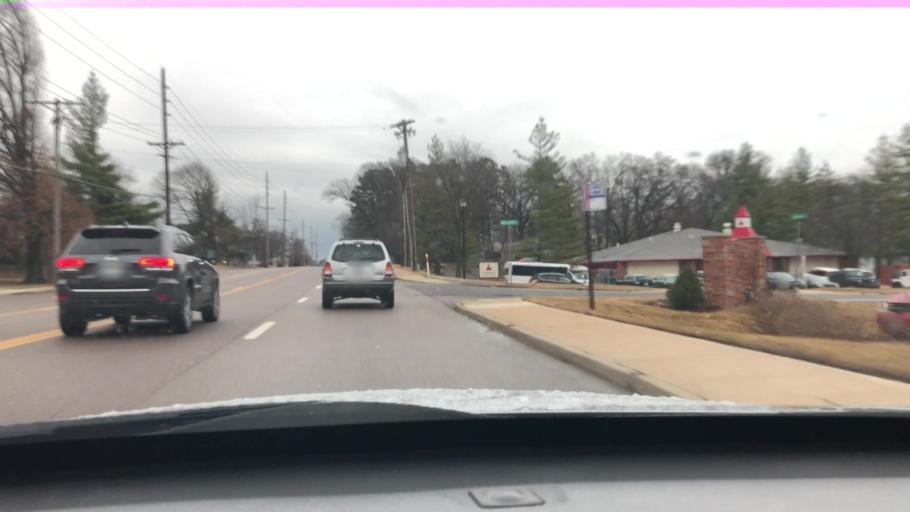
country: US
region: Missouri
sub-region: Saint Louis County
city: Valley Park
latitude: 38.5678
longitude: -90.5074
